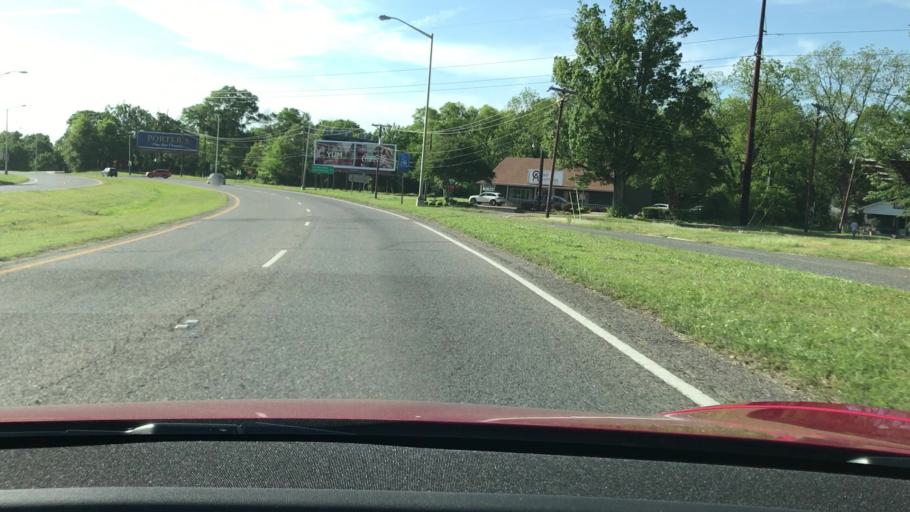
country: US
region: Louisiana
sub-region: Bossier Parish
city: Bossier City
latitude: 32.5029
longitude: -93.7254
